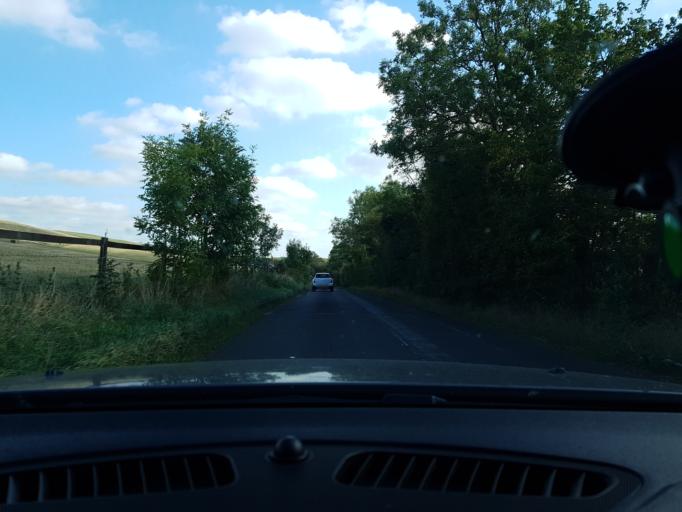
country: GB
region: England
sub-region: Borough of Swindon
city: Bishopstone
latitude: 51.5226
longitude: -1.6586
